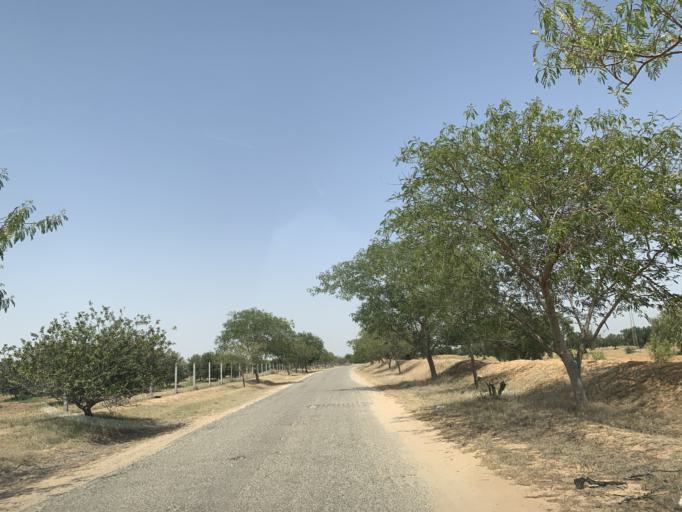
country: TN
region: Al Mahdiyah
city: Shurban
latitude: 35.1923
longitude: 10.2500
